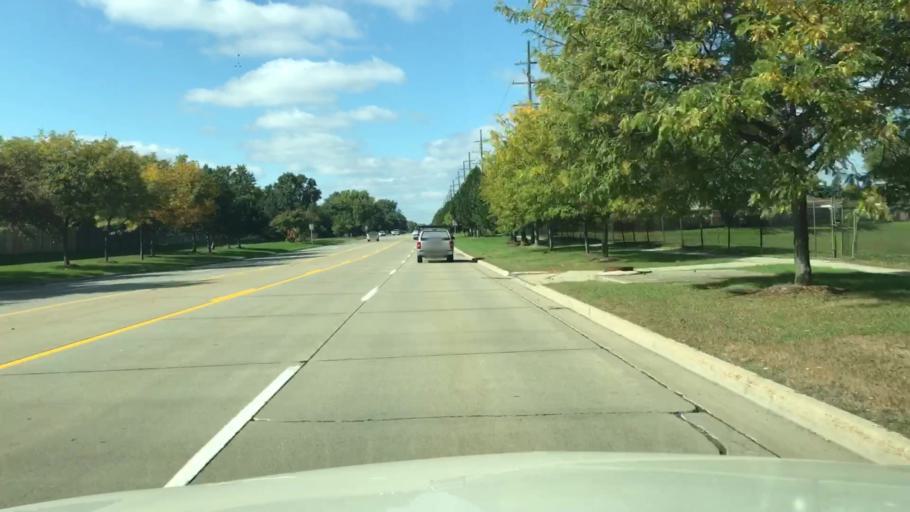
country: US
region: Michigan
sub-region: Macomb County
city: Sterling Heights
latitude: 42.5790
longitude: -83.0777
